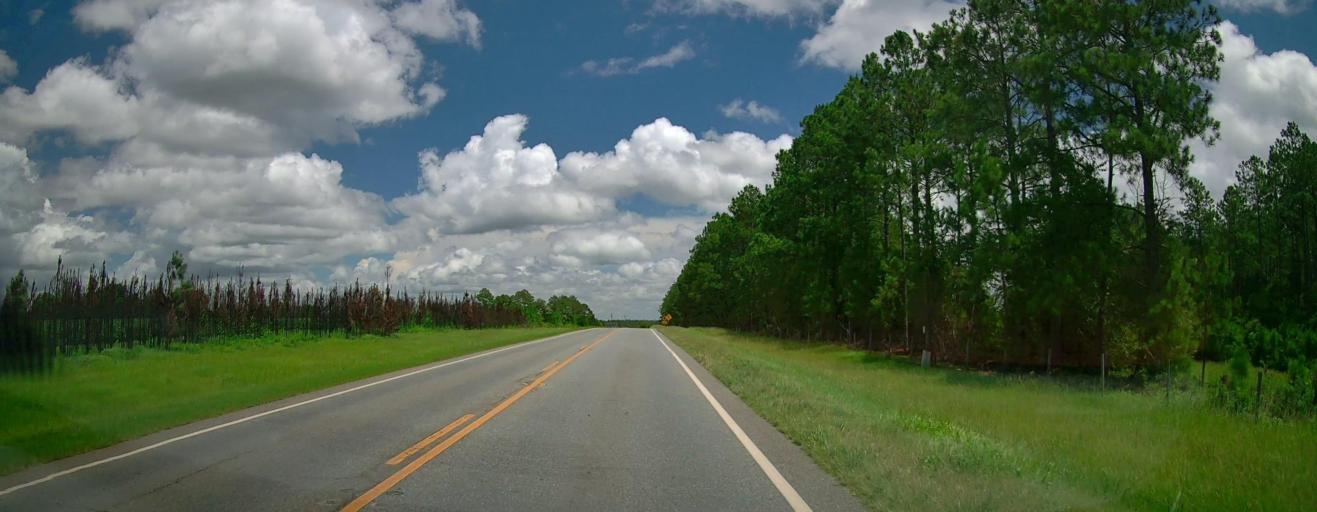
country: US
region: Georgia
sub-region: Turner County
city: Ashburn
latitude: 31.7160
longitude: -83.6151
